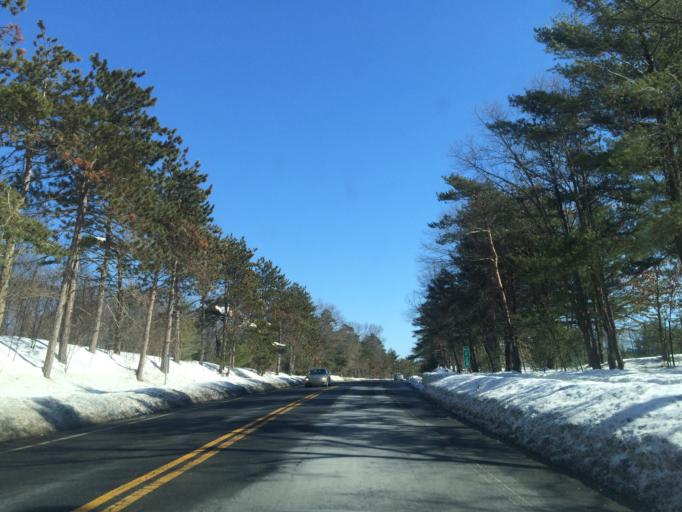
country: US
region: Massachusetts
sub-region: Norfolk County
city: Wellesley
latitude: 42.2952
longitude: -71.3167
